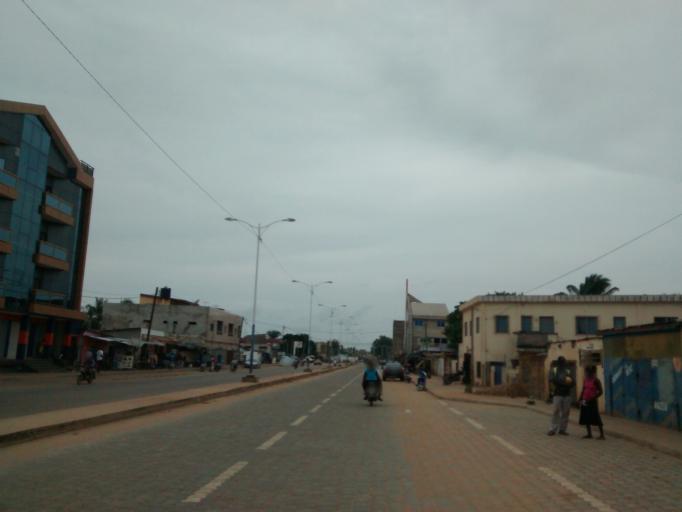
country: TG
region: Maritime
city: Lome
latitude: 6.1785
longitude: 1.1964
